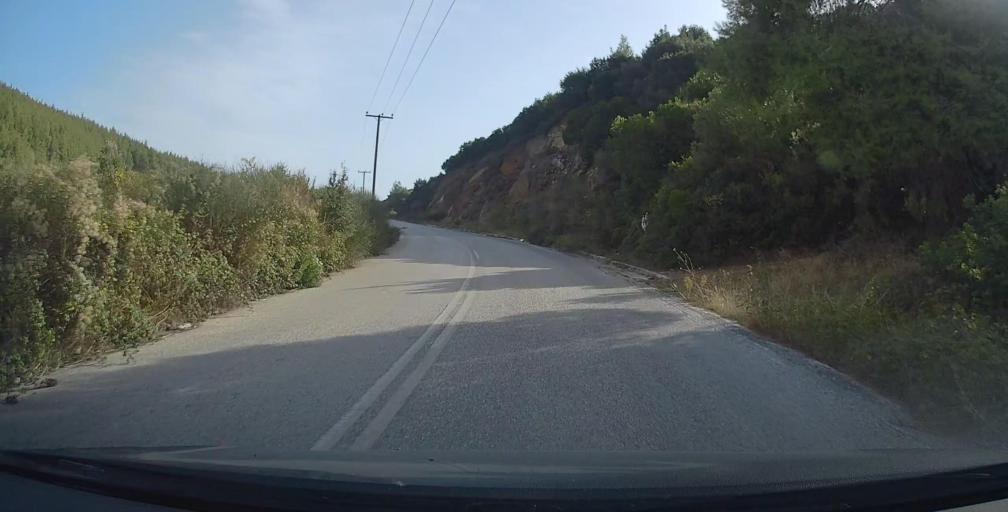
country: GR
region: Central Macedonia
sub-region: Nomos Chalkidikis
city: Sykia
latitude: 39.9598
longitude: 23.9431
